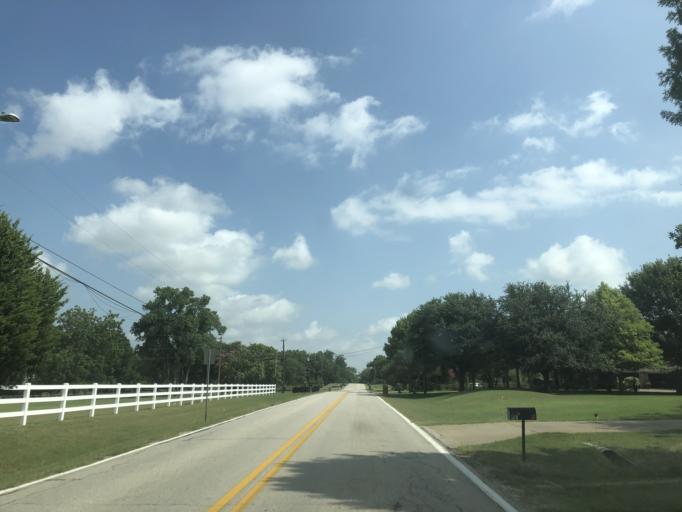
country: US
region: Texas
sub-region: Dallas County
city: Sunnyvale
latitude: 32.8274
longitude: -96.5600
